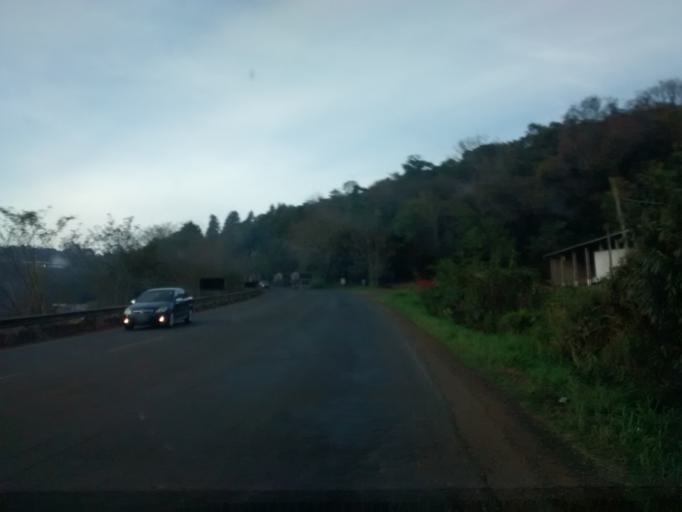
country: BR
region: Parana
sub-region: Francisco Beltrao
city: Francisco Beltrao
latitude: -26.0841
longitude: -53.0700
